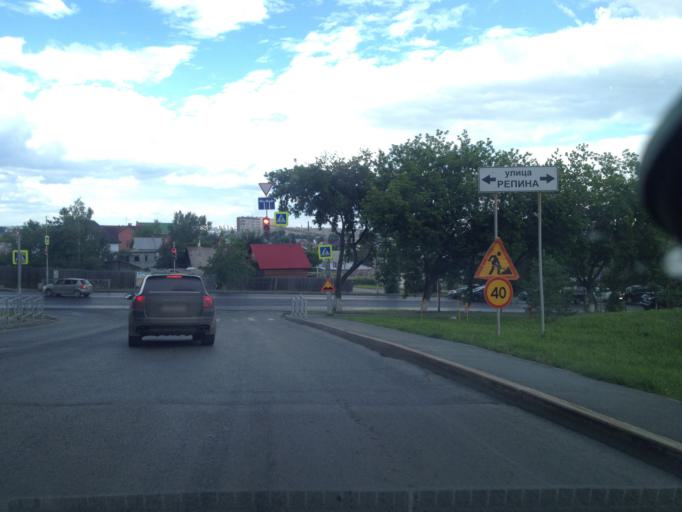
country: RU
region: Sverdlovsk
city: Shirokaya Rechka
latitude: 56.8169
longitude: 60.5340
